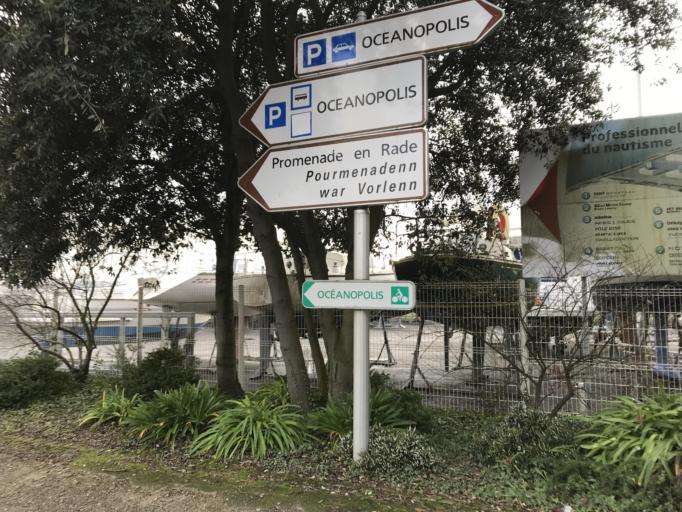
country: FR
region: Brittany
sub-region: Departement du Finistere
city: Brest
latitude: 48.3897
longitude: -4.4387
